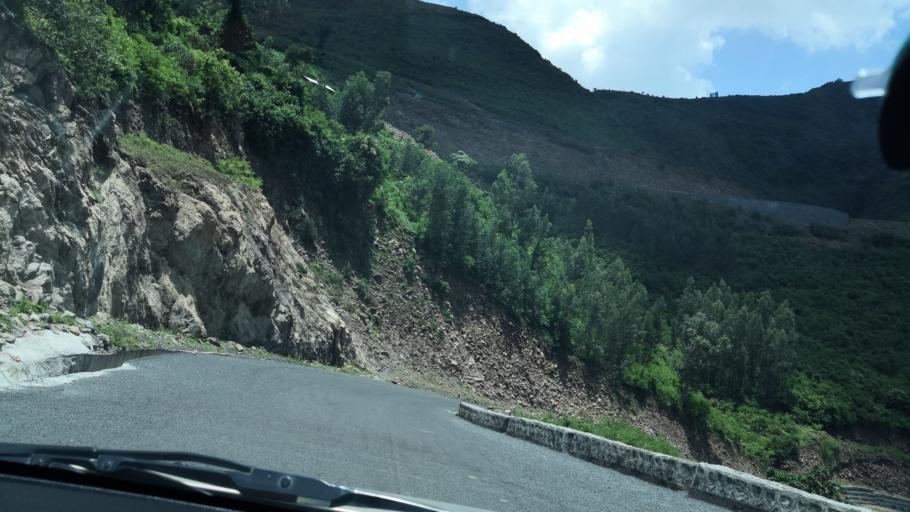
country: ET
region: Amhara
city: Abomsa
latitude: 10.3009
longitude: 39.8895
